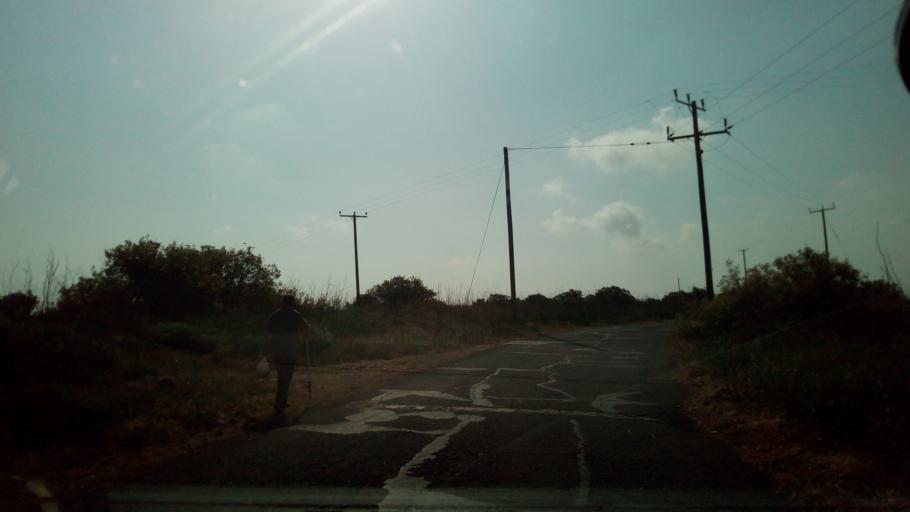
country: CY
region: Pafos
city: Pegeia
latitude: 34.9636
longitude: 32.3841
